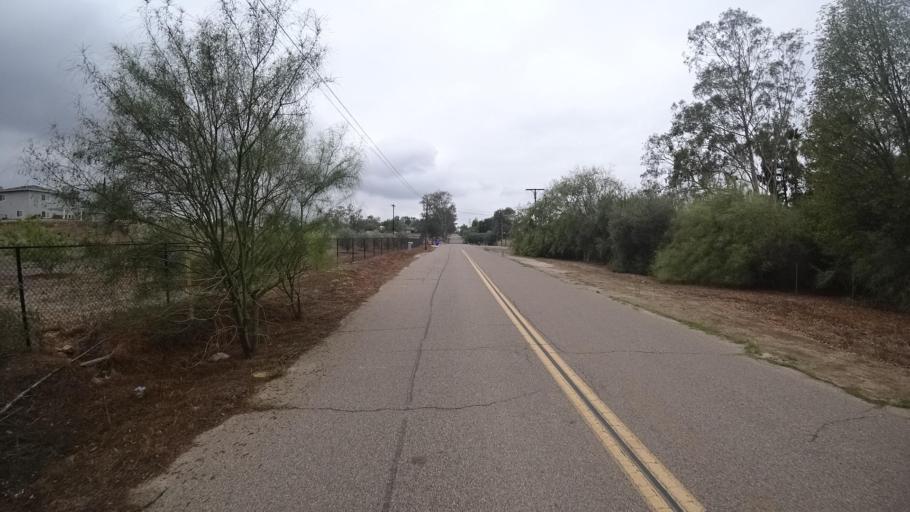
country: US
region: California
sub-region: San Diego County
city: Ramona
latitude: 33.0584
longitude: -116.8663
